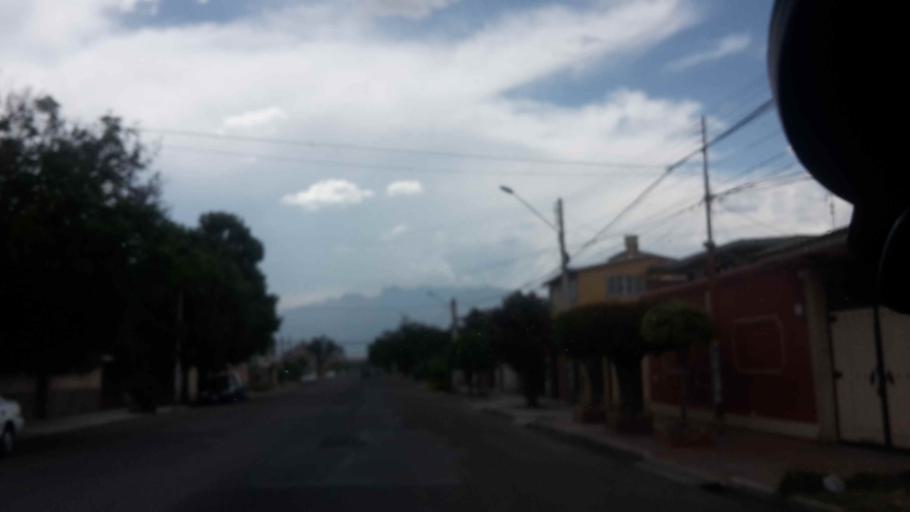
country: BO
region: Cochabamba
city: Cochabamba
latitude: -17.4055
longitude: -66.1733
